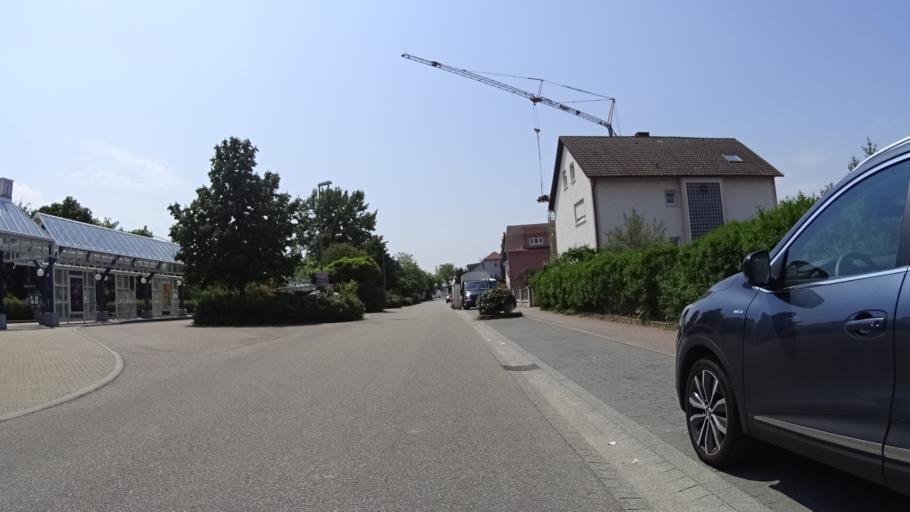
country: DE
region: Baden-Wuerttemberg
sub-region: Karlsruhe Region
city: Eggenstein-Leopoldshafen
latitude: 49.0760
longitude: 8.3978
